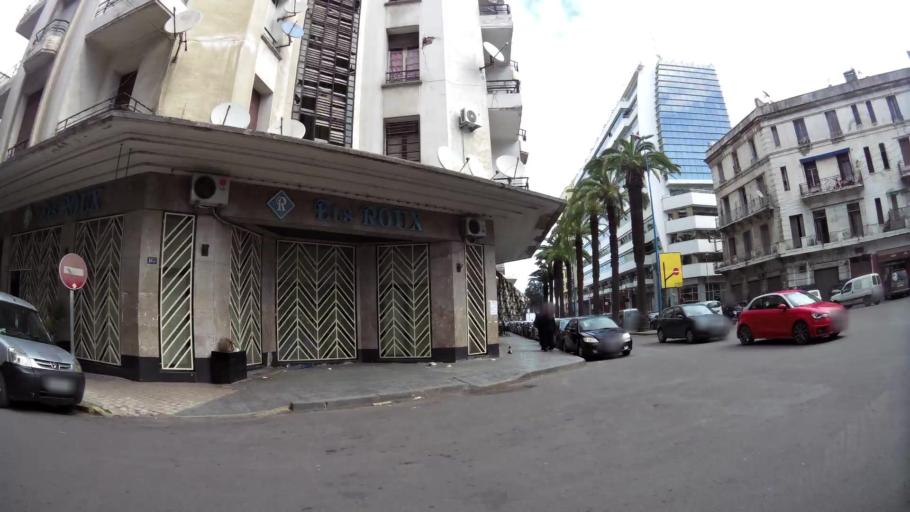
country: MA
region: Grand Casablanca
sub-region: Casablanca
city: Casablanca
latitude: 33.5950
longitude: -7.6104
